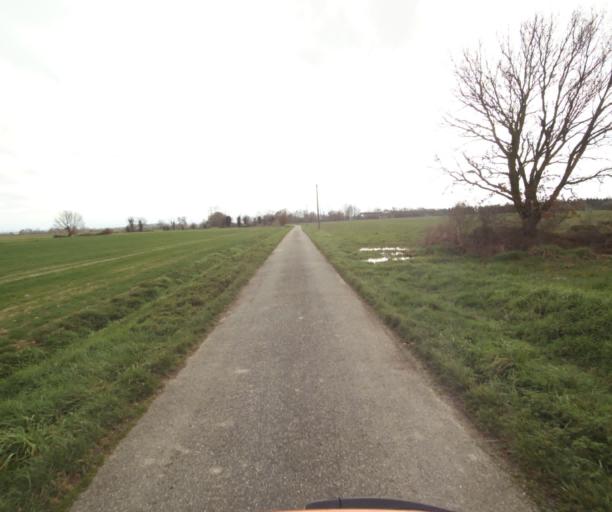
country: FR
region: Midi-Pyrenees
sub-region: Departement de l'Ariege
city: La Tour-du-Crieu
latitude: 43.1644
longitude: 1.6838
